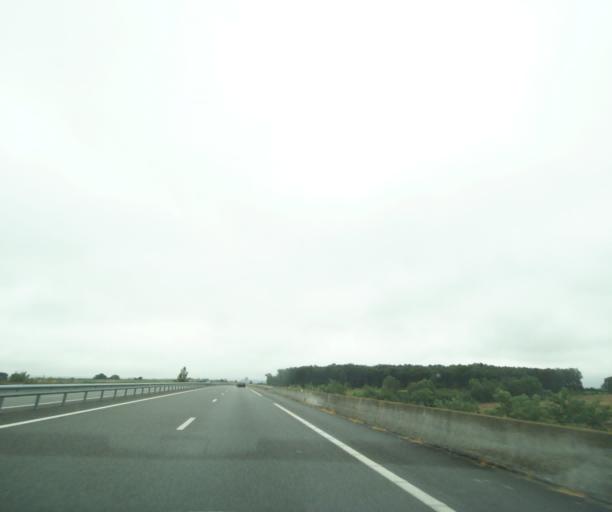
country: FR
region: Midi-Pyrenees
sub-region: Departement du Tarn
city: Le Garric
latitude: 44.0248
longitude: 2.1868
